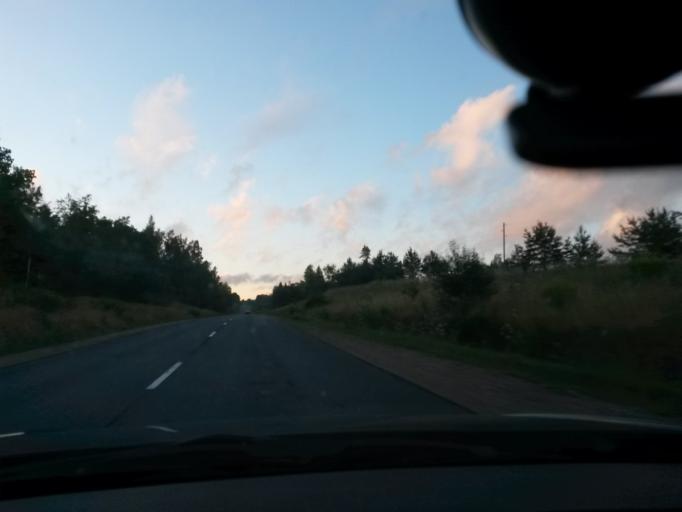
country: LV
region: Madonas Rajons
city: Madona
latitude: 56.7789
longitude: 26.0307
